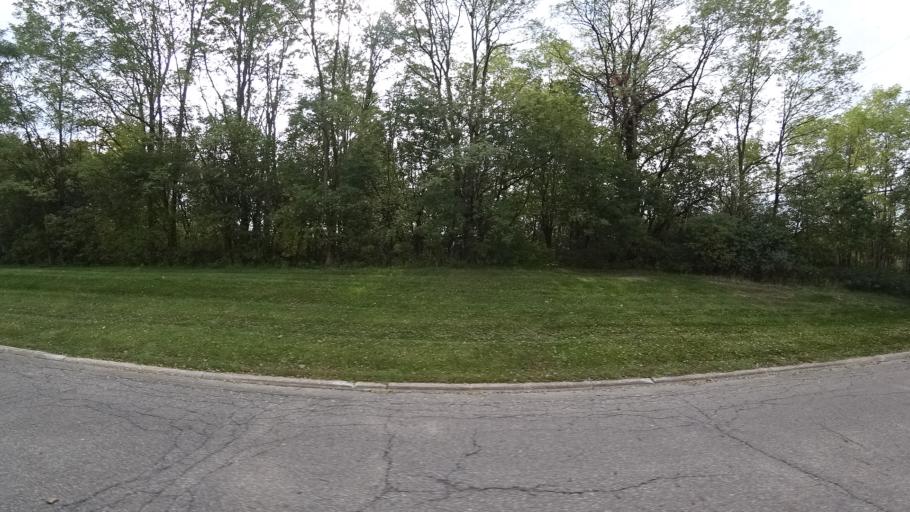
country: US
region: Indiana
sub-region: LaPorte County
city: Michigan City
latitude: 41.6687
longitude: -86.8985
